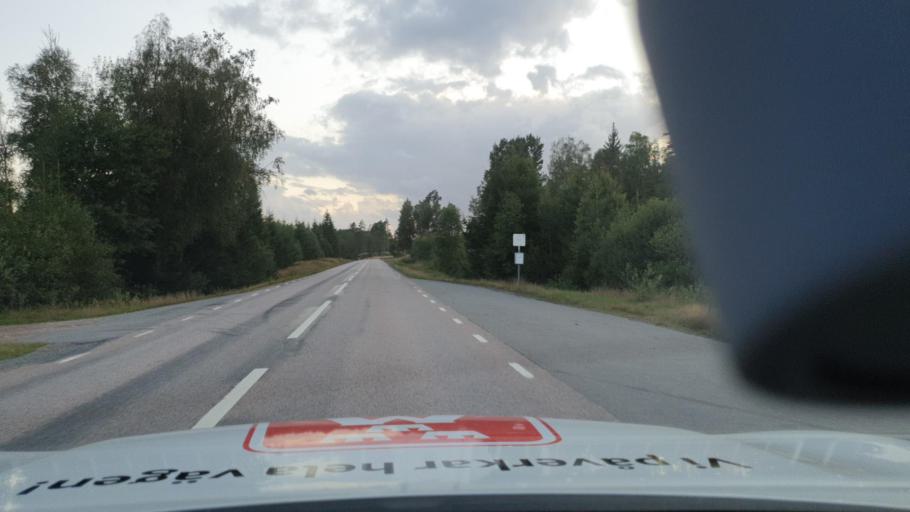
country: SE
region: Vaestra Goetaland
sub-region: Marks Kommun
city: Fritsla
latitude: 57.5009
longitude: 12.9146
